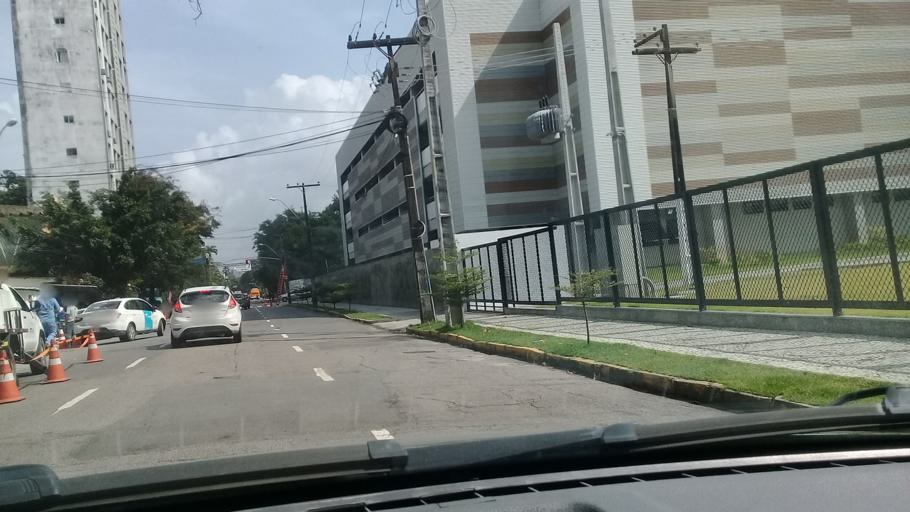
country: BR
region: Pernambuco
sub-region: Recife
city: Recife
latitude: -8.0571
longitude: -34.8790
